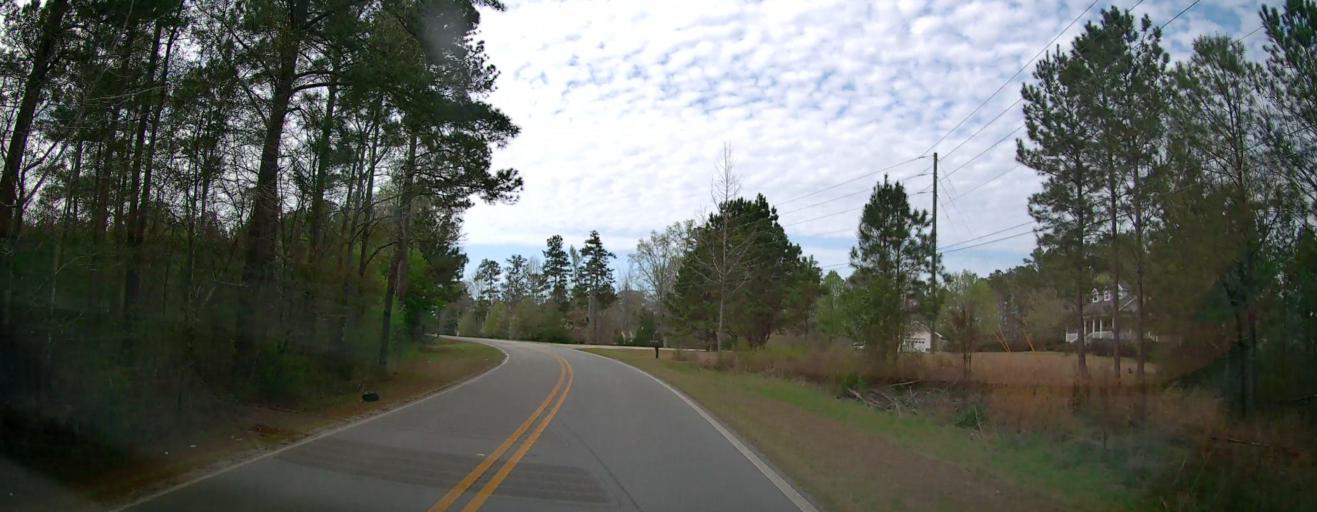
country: US
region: Georgia
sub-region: Bibb County
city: Macon
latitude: 32.9556
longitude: -83.6536
